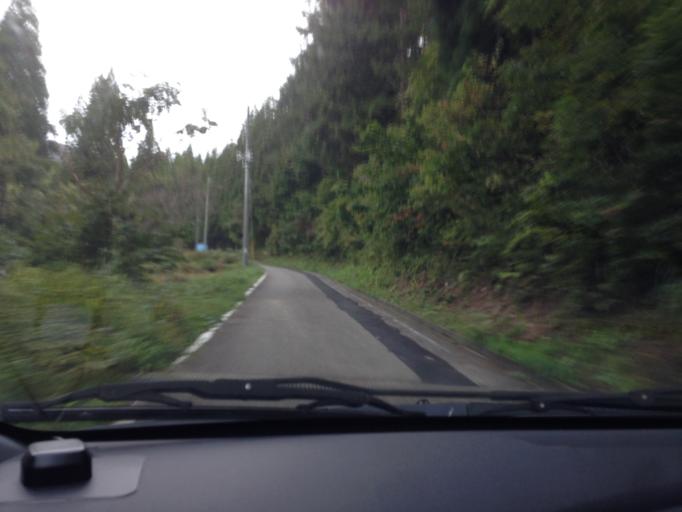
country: JP
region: Fukushima
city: Kitakata
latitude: 37.3901
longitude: 139.6124
